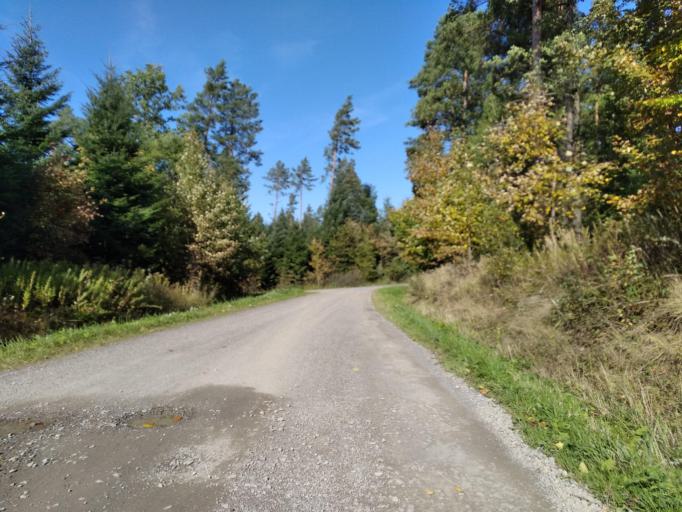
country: PL
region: Subcarpathian Voivodeship
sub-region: Powiat strzyzowski
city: Wysoka Strzyzowska
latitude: 49.8151
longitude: 21.7892
